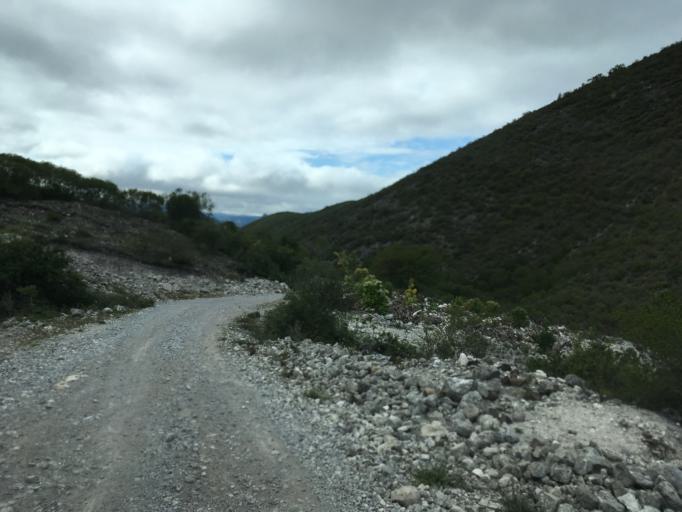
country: MX
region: Hidalgo
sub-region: Metztitlan
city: Fontezuelas
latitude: 20.6226
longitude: -98.8680
